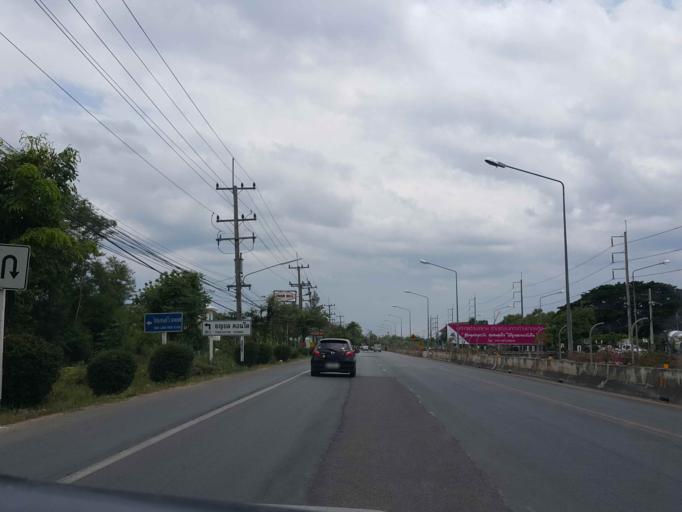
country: TH
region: Chiang Mai
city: Chiang Mai
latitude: 18.7731
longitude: 98.9515
